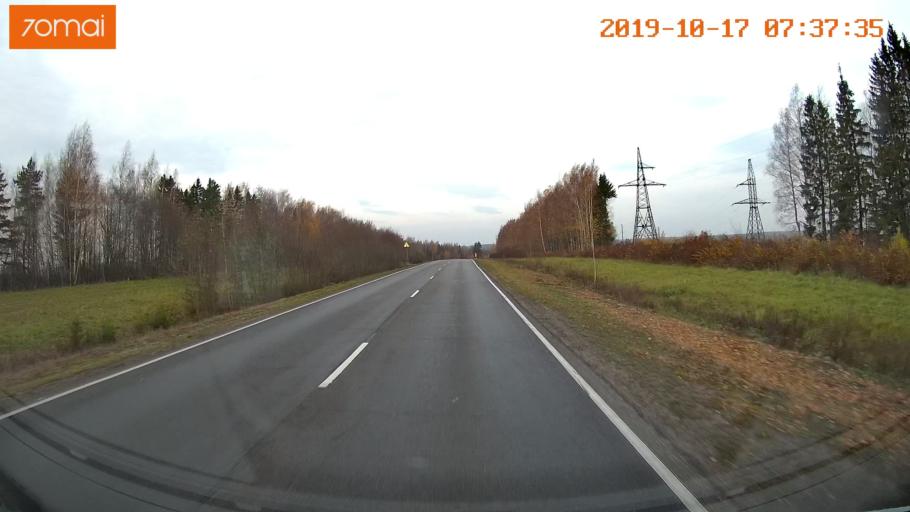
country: RU
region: Vladimir
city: Yur'yev-Pol'skiy
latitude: 56.4501
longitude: 39.8955
